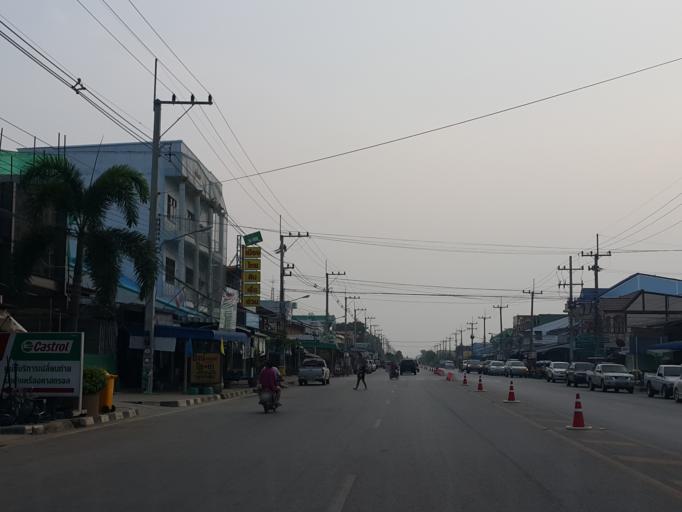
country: TH
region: Uthai Thani
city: Huai Khot
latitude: 15.1768
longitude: 99.6971
